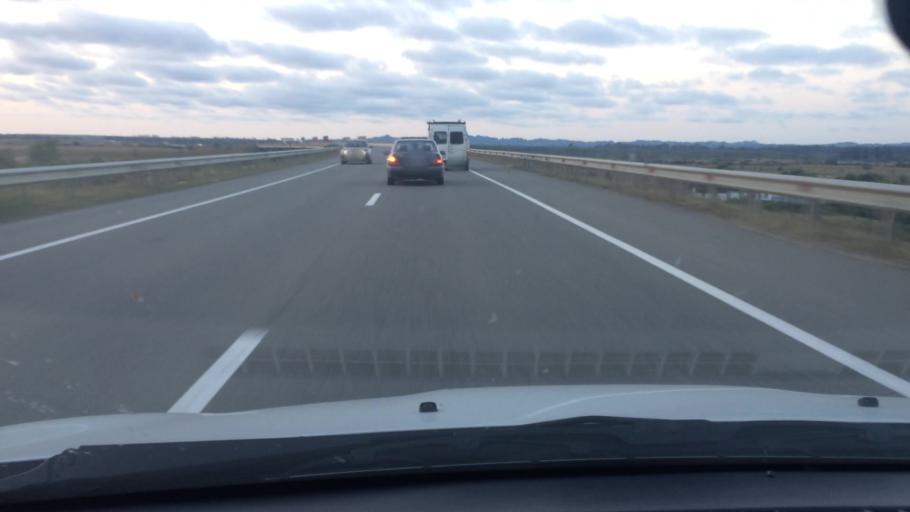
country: GE
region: Ajaria
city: Ochkhamuri
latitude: 41.8638
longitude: 41.8373
